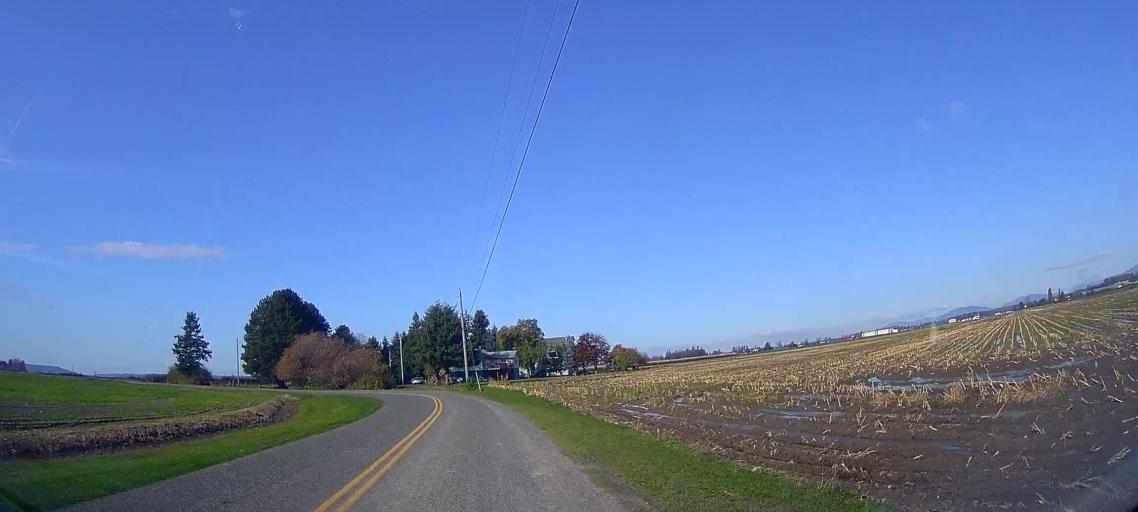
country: US
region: Washington
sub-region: Snohomish County
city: Stanwood
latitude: 48.3294
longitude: -122.3691
